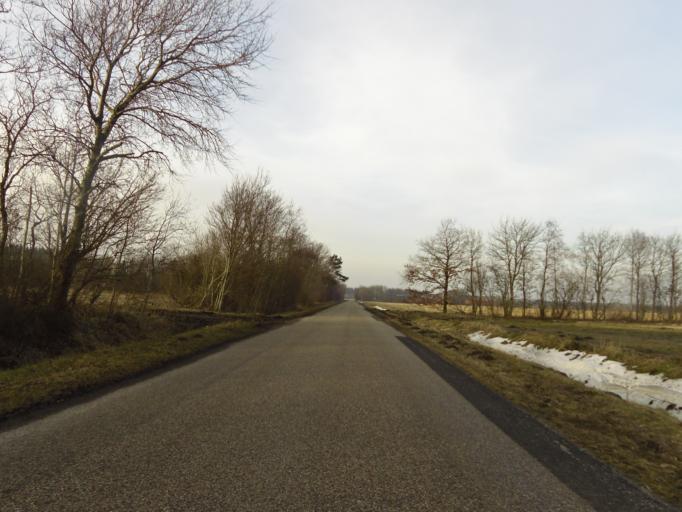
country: DK
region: South Denmark
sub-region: Tonder Kommune
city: Logumkloster
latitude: 55.1560
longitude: 8.8993
